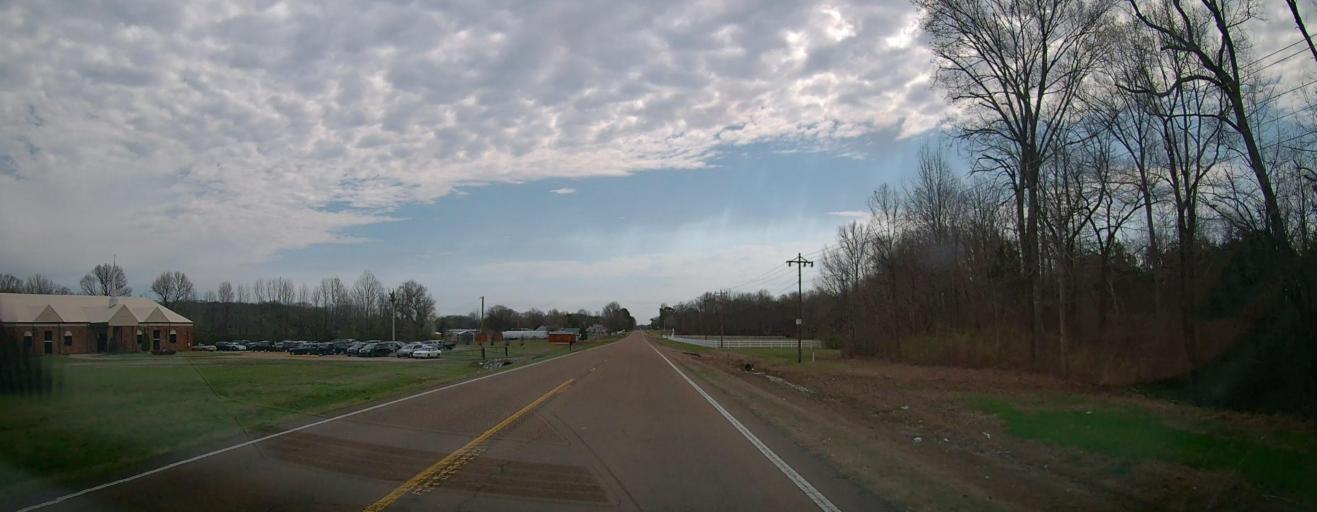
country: US
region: Mississippi
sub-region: Marshall County
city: Byhalia
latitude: 34.8577
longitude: -89.6477
